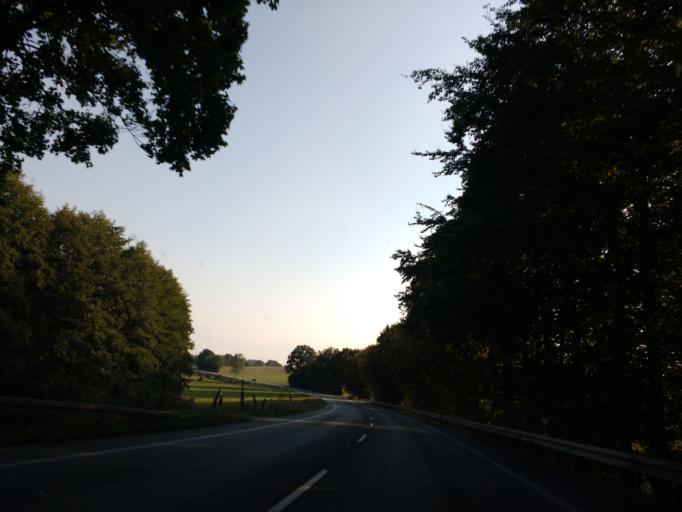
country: DE
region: North Rhine-Westphalia
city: Brakel
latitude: 51.6406
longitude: 9.1362
